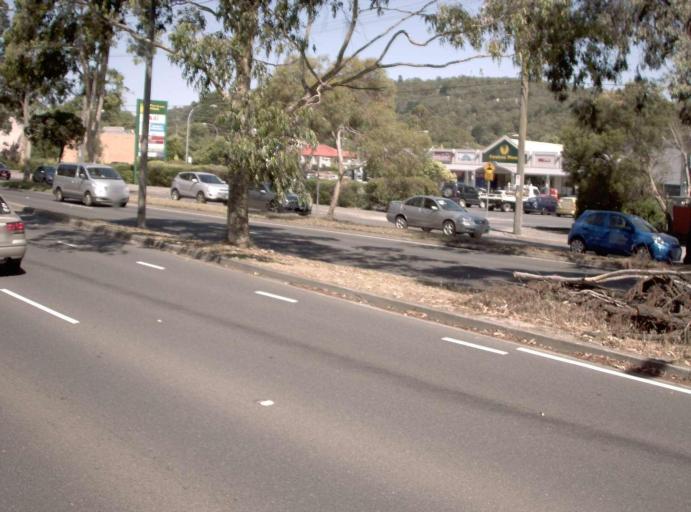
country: AU
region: Victoria
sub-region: Knox
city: Ferntree Gully
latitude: -37.8933
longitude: 145.3077
